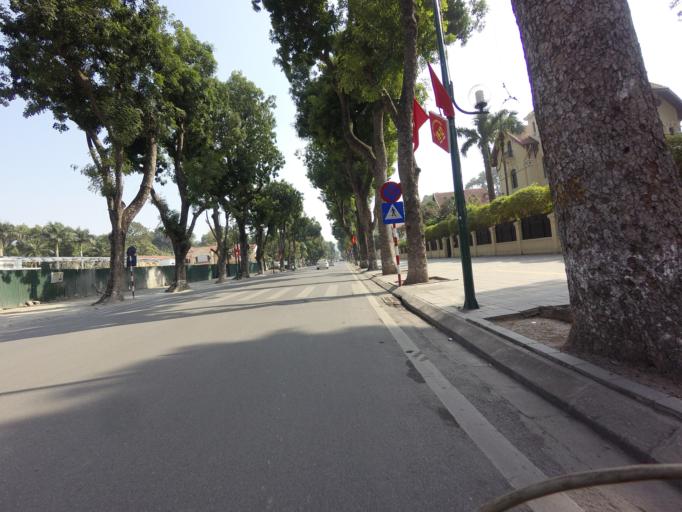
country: VN
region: Ha Noi
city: Hanoi
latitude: 21.0348
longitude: 105.8370
